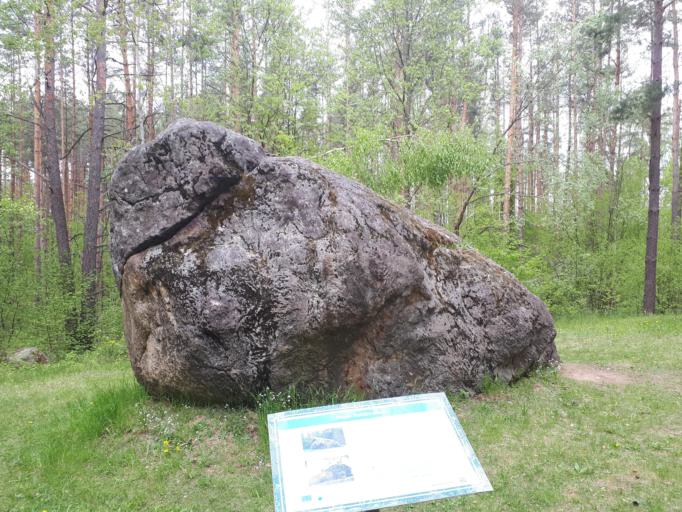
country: LT
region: Alytaus apskritis
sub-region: Alytus
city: Alytus
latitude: 54.2725
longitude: 24.0200
